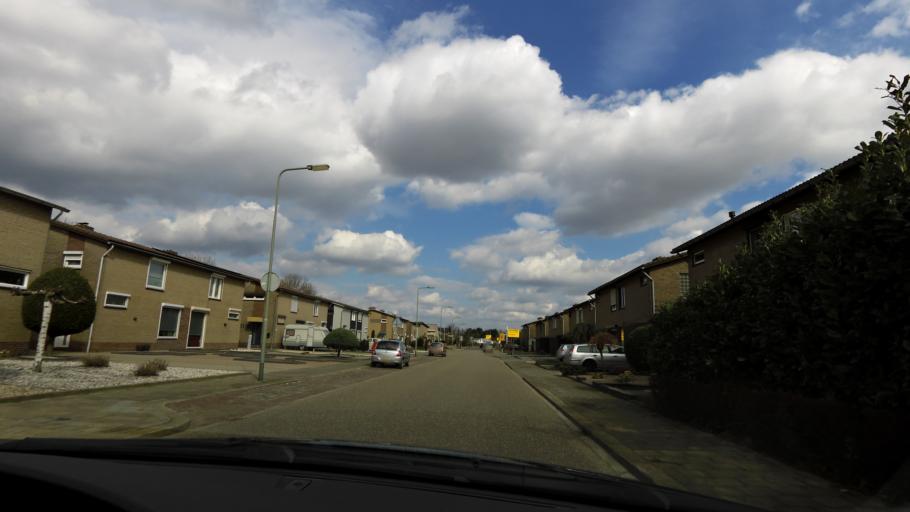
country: NL
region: Limburg
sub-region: Gemeente Sittard-Geleen
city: Limbricht
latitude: 51.0397
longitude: 5.8608
